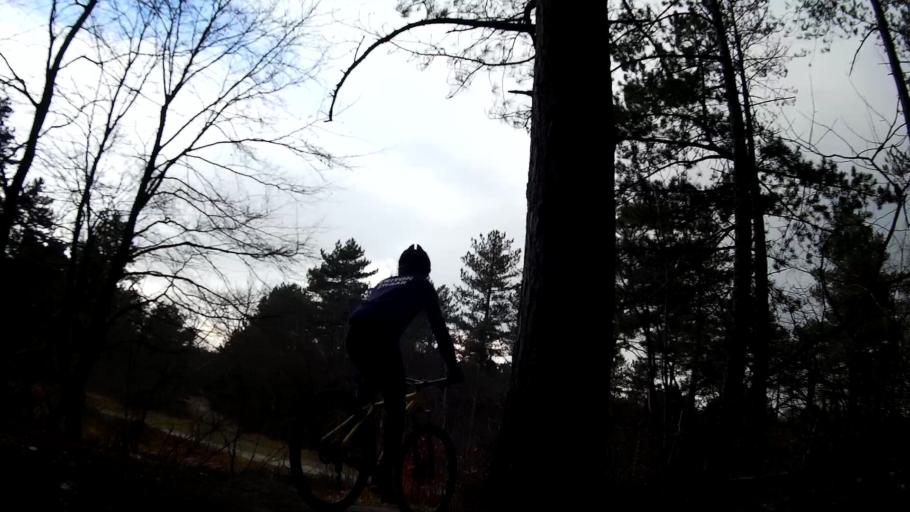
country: NL
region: North Holland
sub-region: Gemeente Bergen
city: Egmond aan Zee
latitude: 52.6921
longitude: 4.6678
